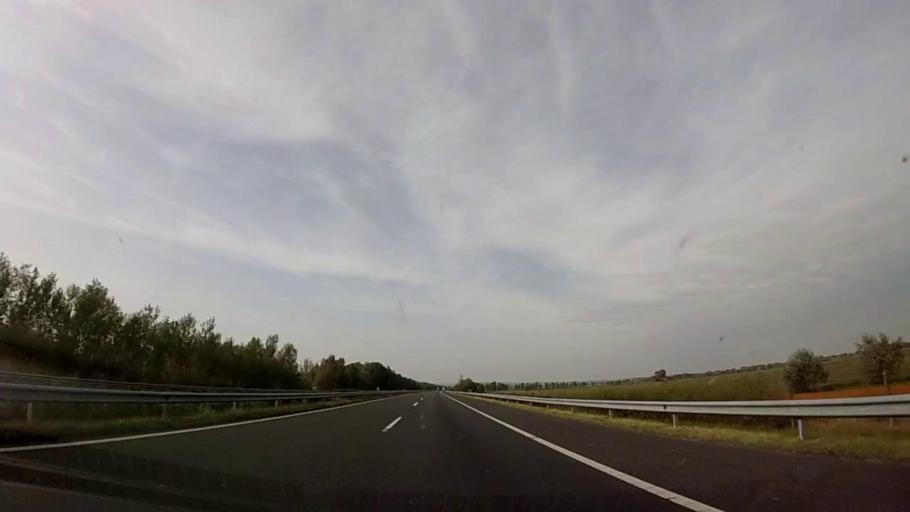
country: HU
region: Somogy
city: Kethely
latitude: 46.6909
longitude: 17.4356
